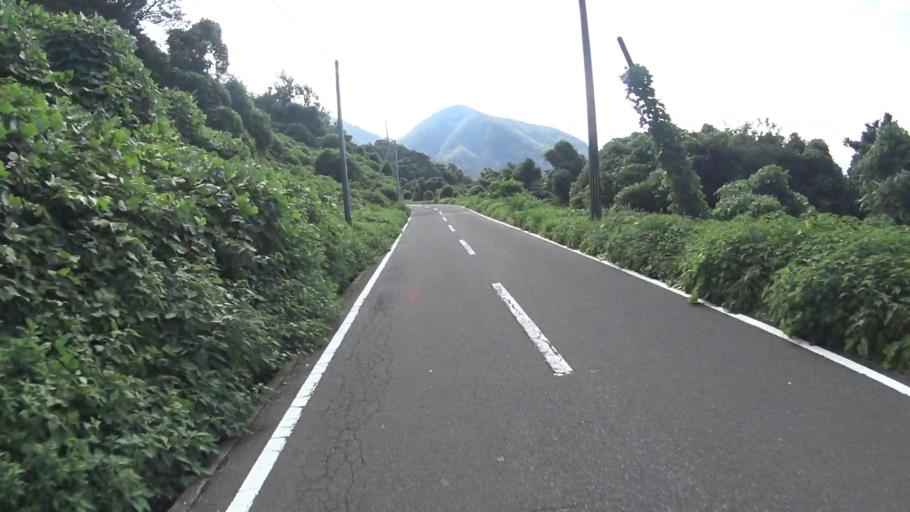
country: JP
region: Kyoto
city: Miyazu
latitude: 35.7675
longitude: 135.2155
